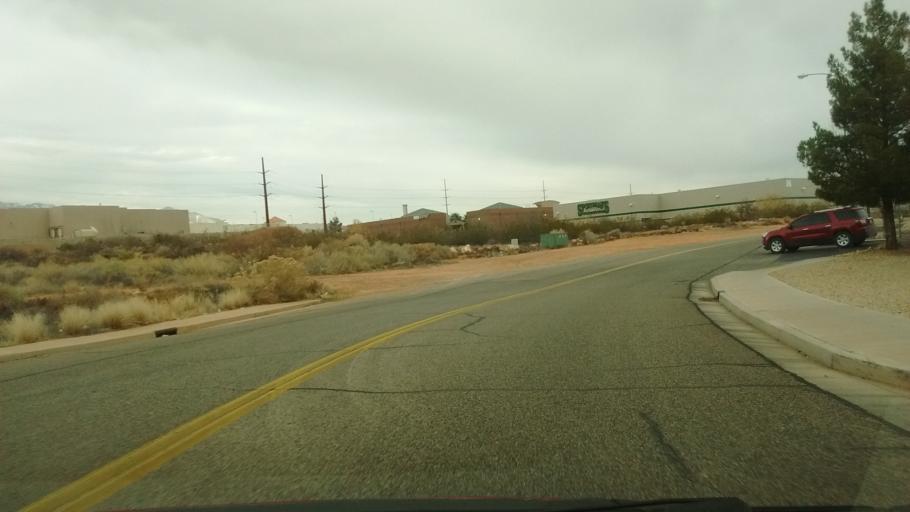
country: US
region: Utah
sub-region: Washington County
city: Washington
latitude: 37.1231
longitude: -113.5251
